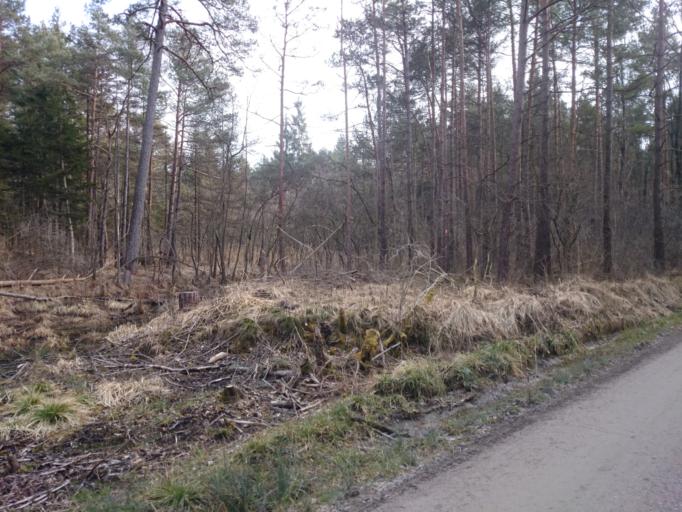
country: DE
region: Bavaria
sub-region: Swabia
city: Konigsbrunn
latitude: 48.2843
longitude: 10.9139
